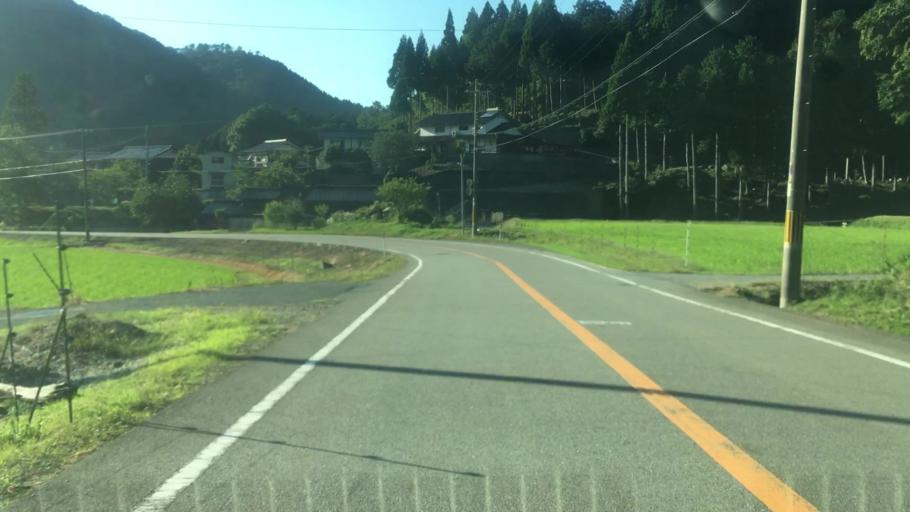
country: JP
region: Hyogo
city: Toyooka
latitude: 35.6213
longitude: 134.8667
